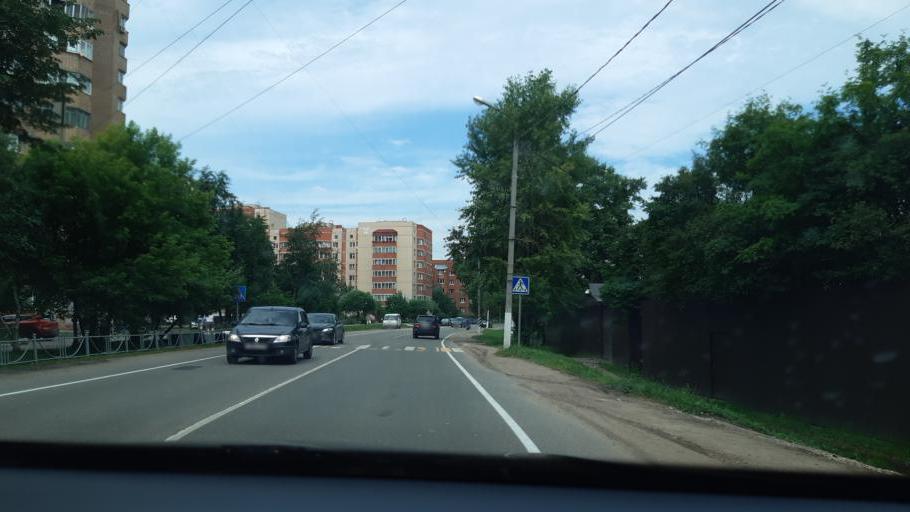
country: RU
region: Moskovskaya
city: Bol'shiye Vyazemy
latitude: 55.6239
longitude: 36.9835
